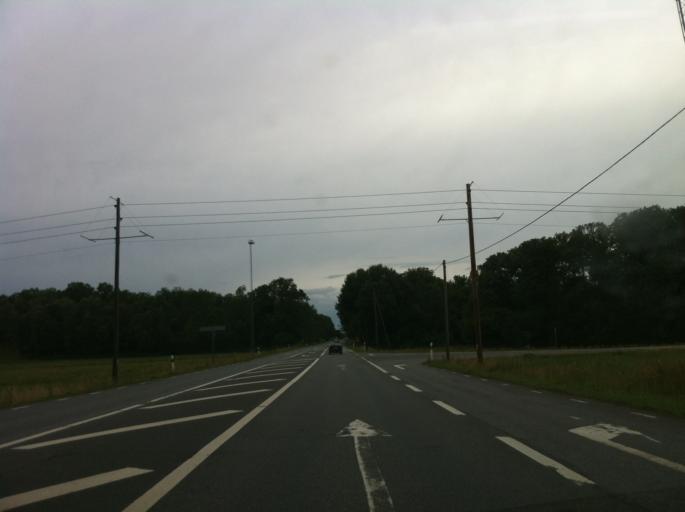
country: SE
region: Skane
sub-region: Hassleholms Kommun
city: Sosdala
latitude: 56.0429
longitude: 13.7048
